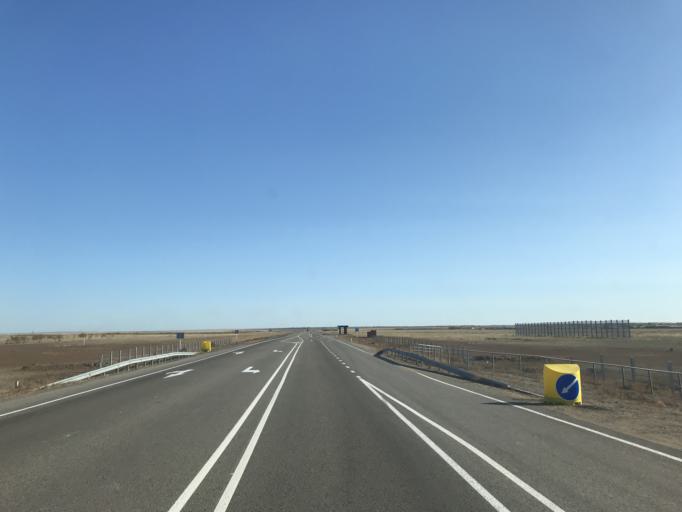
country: KZ
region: Pavlodar
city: Koktobe
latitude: 51.8970
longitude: 77.3925
